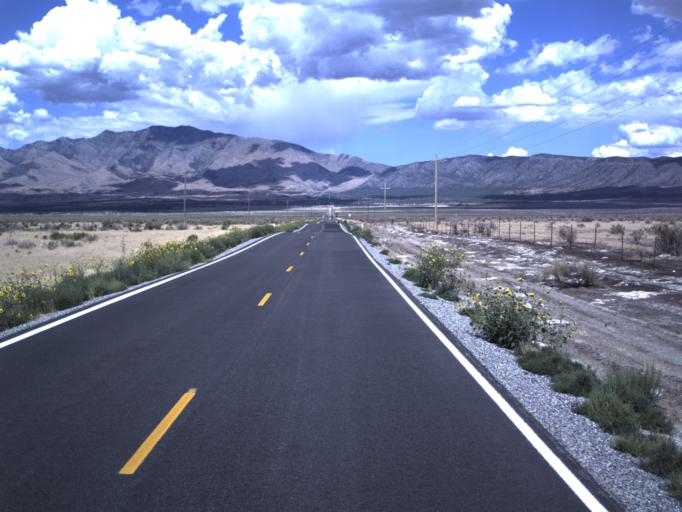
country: US
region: Utah
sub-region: Tooele County
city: Grantsville
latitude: 40.2578
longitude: -112.6953
